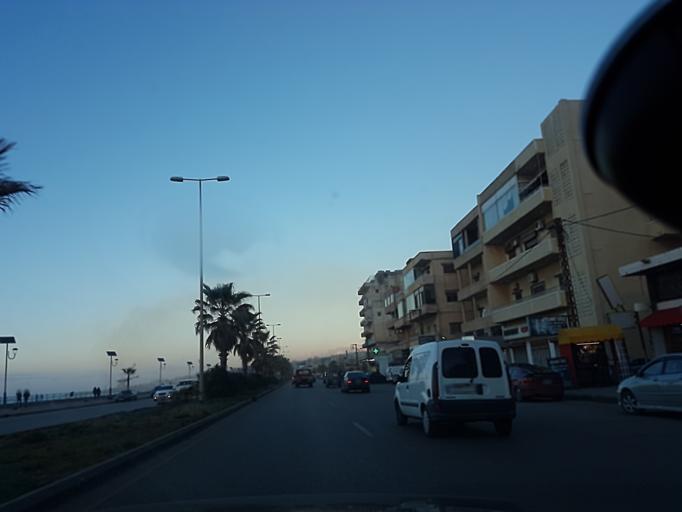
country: LB
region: Liban-Sud
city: Sidon
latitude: 33.5744
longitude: 35.3804
